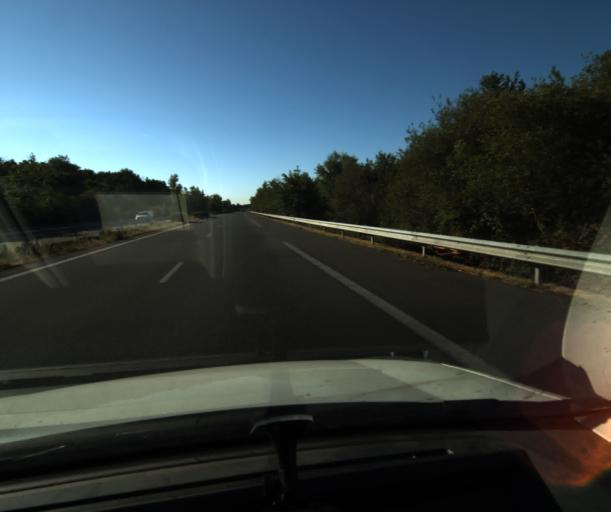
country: FR
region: Midi-Pyrenees
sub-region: Departement du Tarn-et-Garonne
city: Montech
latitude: 43.9737
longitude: 1.2643
